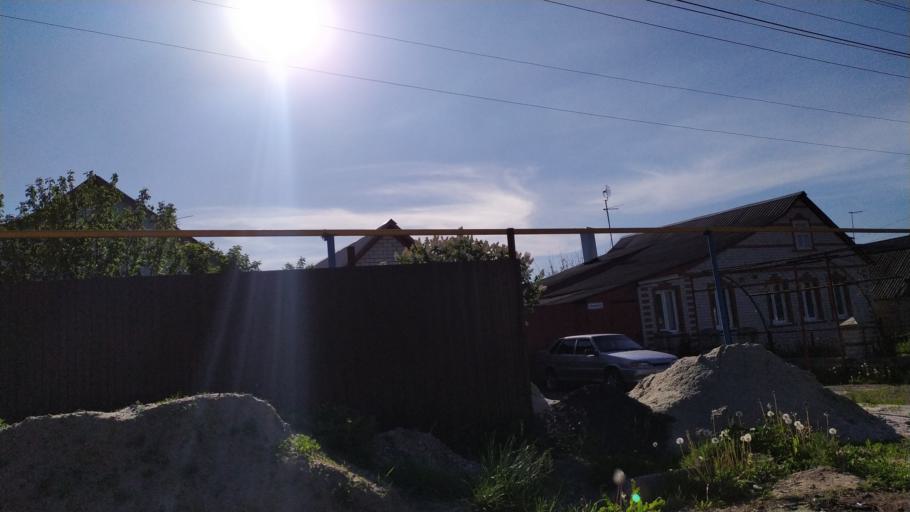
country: RU
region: Kursk
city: Kursk
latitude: 51.6394
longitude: 36.1482
